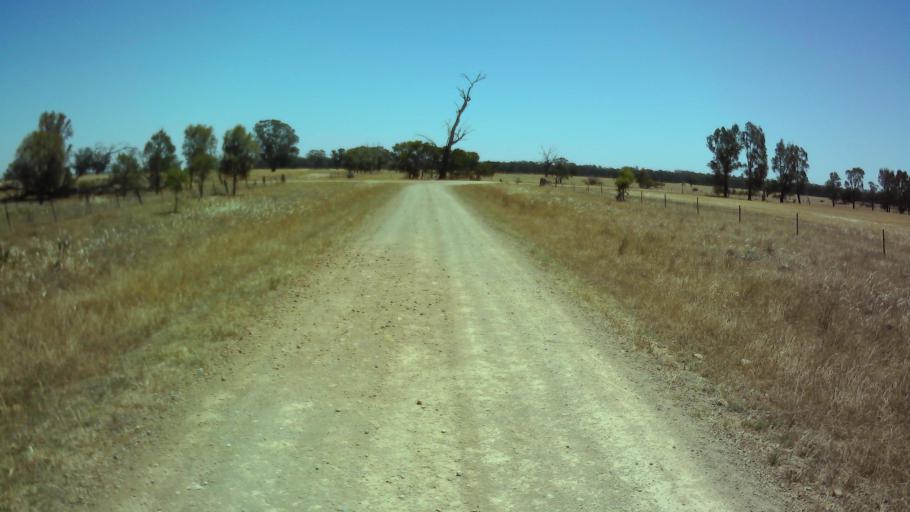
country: AU
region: New South Wales
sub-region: Weddin
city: Grenfell
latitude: -33.9858
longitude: 147.9284
